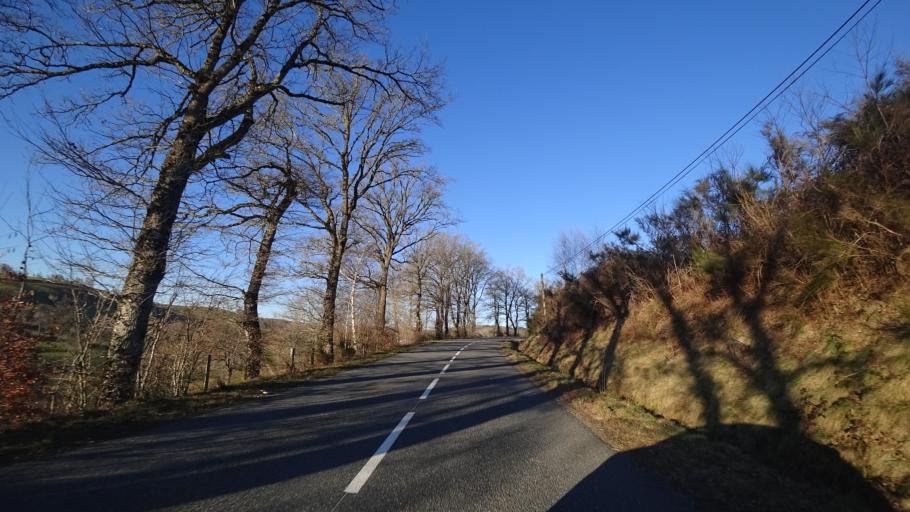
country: FR
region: Midi-Pyrenees
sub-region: Departement de l'Aveyron
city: Pont-de-Salars
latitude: 44.3232
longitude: 2.7574
